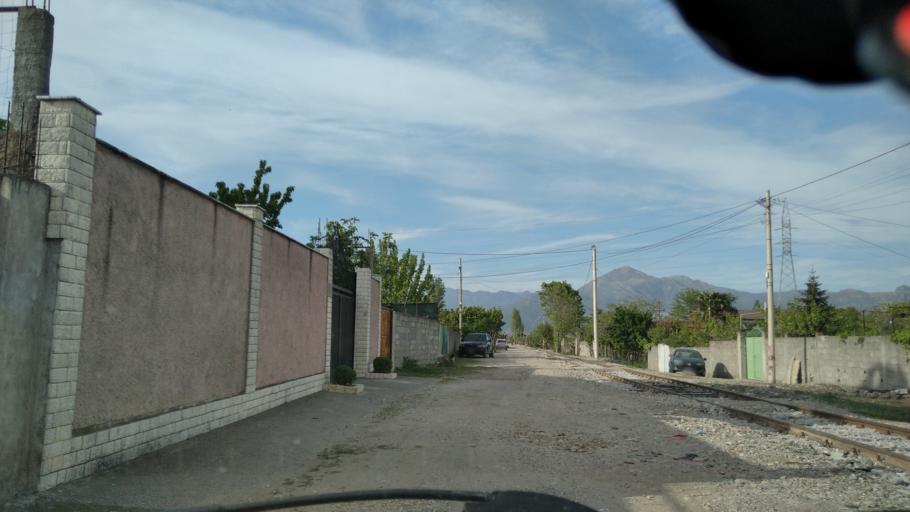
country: AL
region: Shkoder
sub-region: Rrethi i Shkodres
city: Shkoder
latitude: 42.0705
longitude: 19.5291
